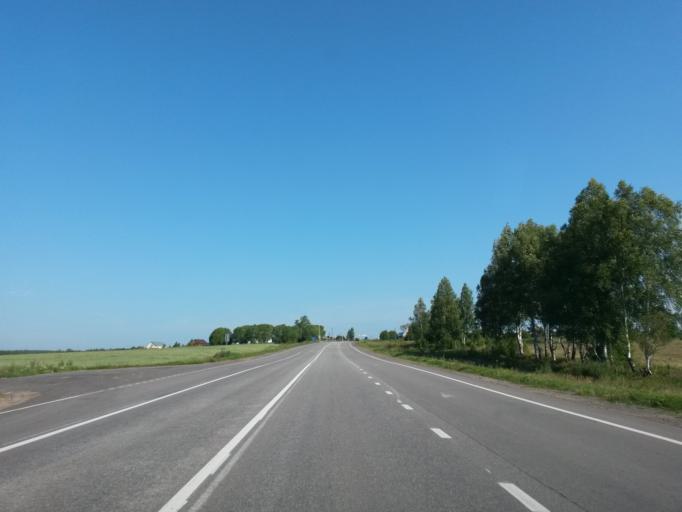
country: RU
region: Jaroslavl
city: Gavrilov-Yam
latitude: 57.3444
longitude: 39.9115
